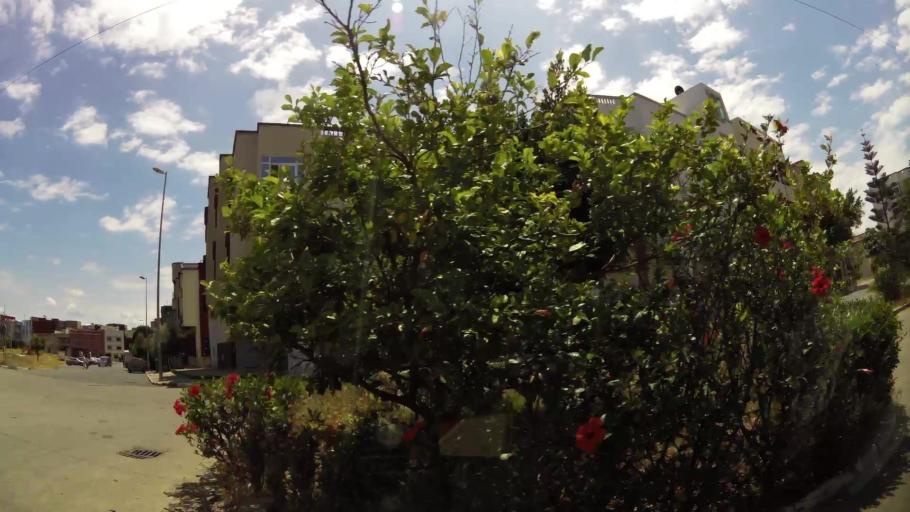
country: MA
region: Gharb-Chrarda-Beni Hssen
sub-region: Kenitra Province
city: Kenitra
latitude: 34.2696
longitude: -6.6147
